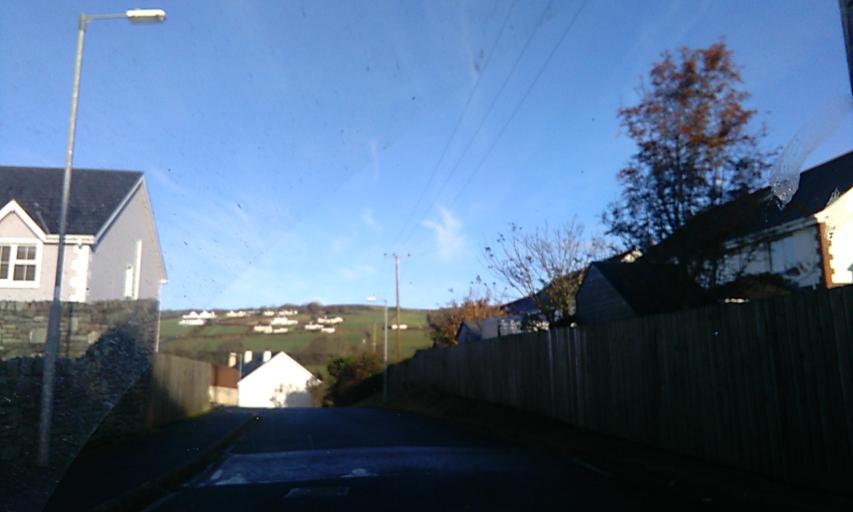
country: IE
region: Ulster
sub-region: County Donegal
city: Moville
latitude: 55.2073
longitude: -6.9722
